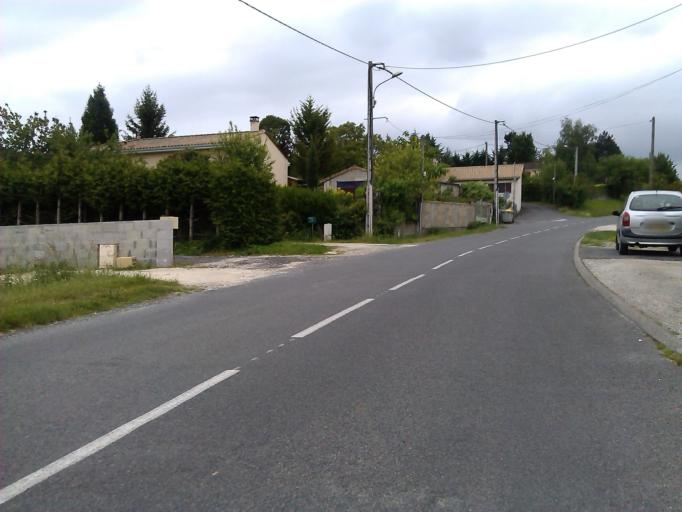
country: FR
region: Poitou-Charentes
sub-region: Departement de la Charente
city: Chateauneuf-sur-Charente
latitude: 45.5897
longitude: -0.0518
